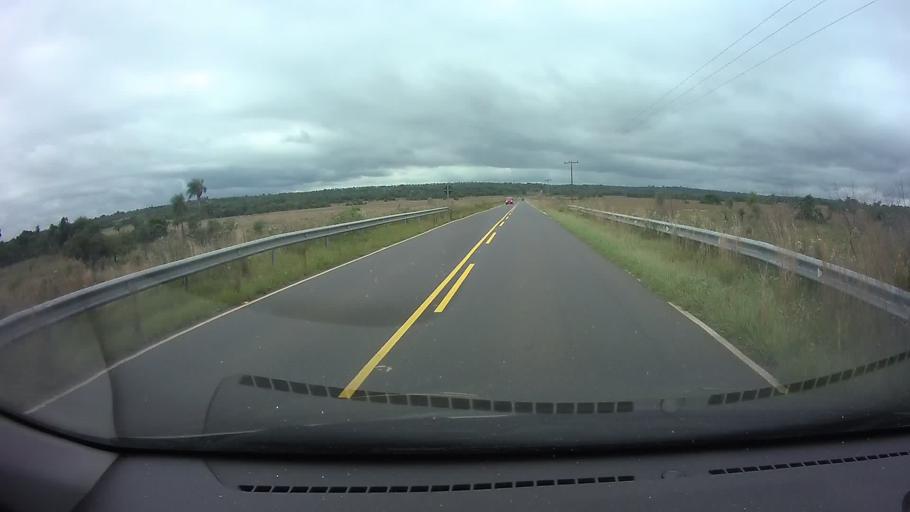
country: PY
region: Paraguari
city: Yaguaron
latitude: -25.7094
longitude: -57.3477
